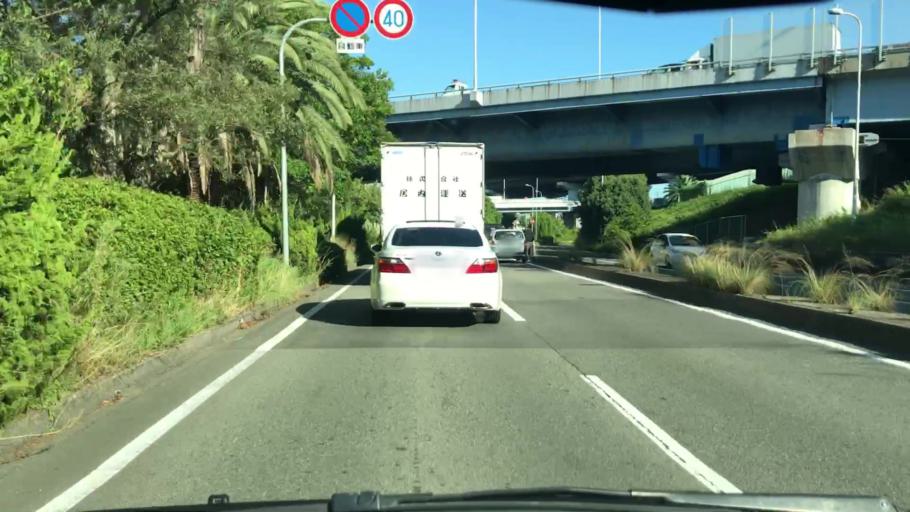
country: JP
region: Osaka
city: Ikeda
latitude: 34.7993
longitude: 135.4397
